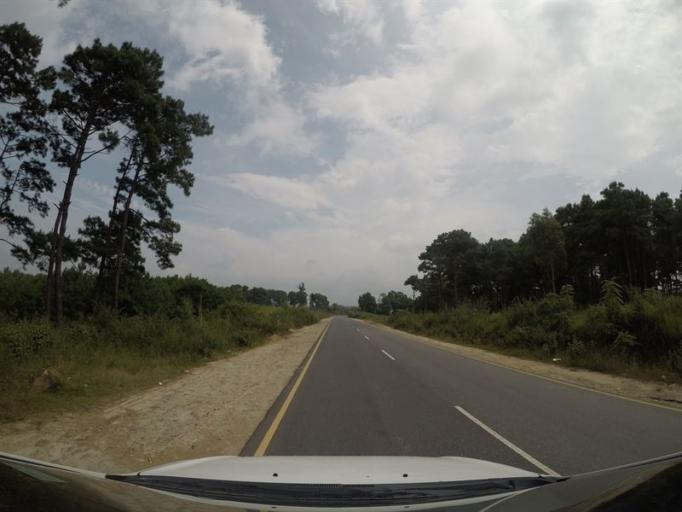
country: IN
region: Meghalaya
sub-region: East Khasi Hills
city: Shillong
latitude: 25.4894
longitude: 92.1901
